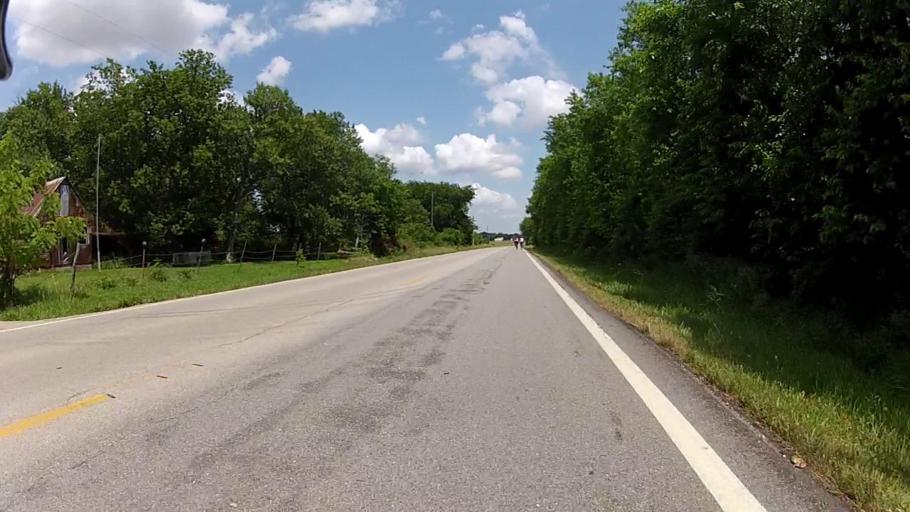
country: US
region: Kansas
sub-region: Labette County
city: Altamont
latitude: 37.1930
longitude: -95.3259
